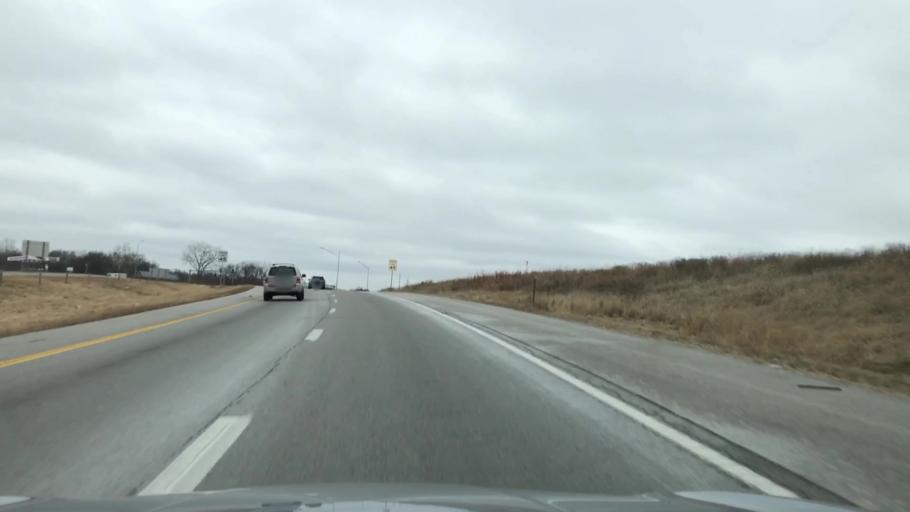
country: US
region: Missouri
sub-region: Jackson County
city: East Independence
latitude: 39.0590
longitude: -94.3689
